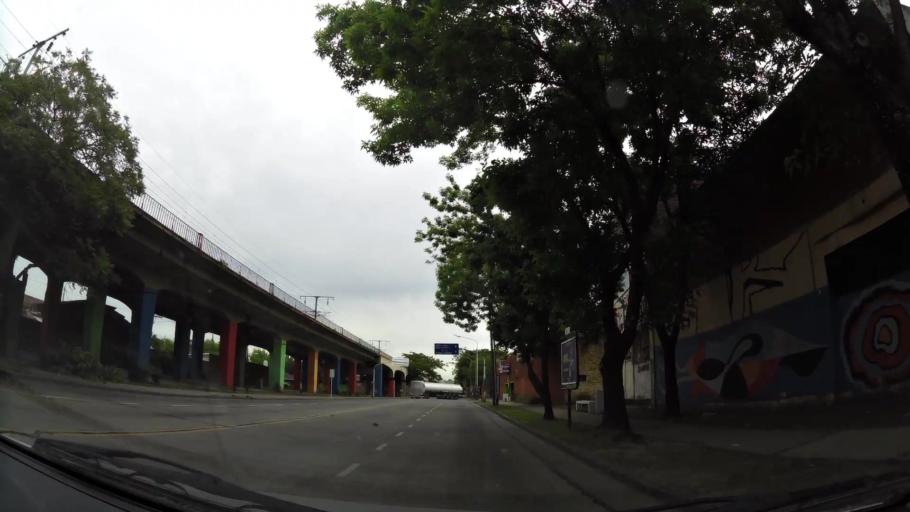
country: AR
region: Buenos Aires
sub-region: Partido de Avellaneda
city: Avellaneda
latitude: -34.6772
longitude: -58.3507
